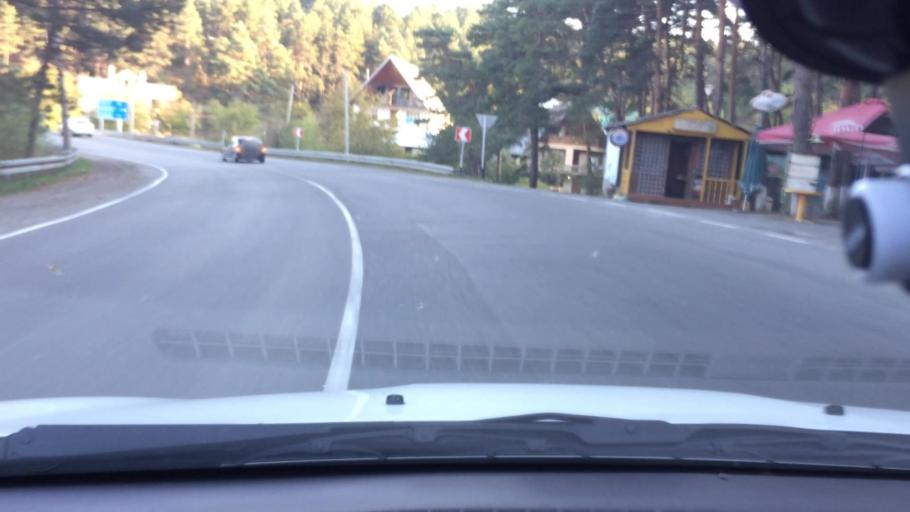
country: GE
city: Surami
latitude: 42.0228
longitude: 43.5668
